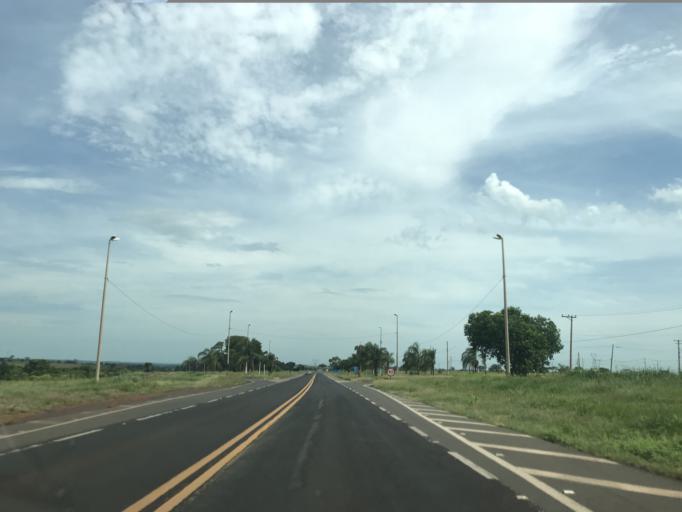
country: BR
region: Sao Paulo
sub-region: Nova Granada
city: Nova Granada
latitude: -20.3506
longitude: -49.2145
